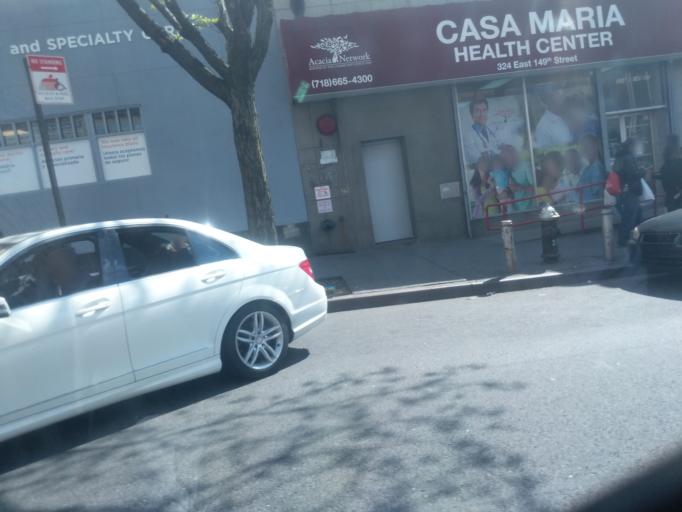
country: US
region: New York
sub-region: New York County
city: Inwood
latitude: 40.8168
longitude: -73.9207
